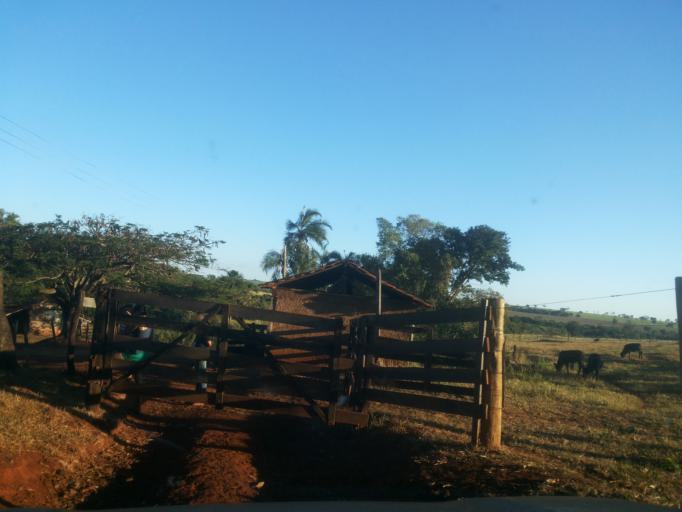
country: BR
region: Minas Gerais
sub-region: Centralina
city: Centralina
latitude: -18.7647
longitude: -49.2018
